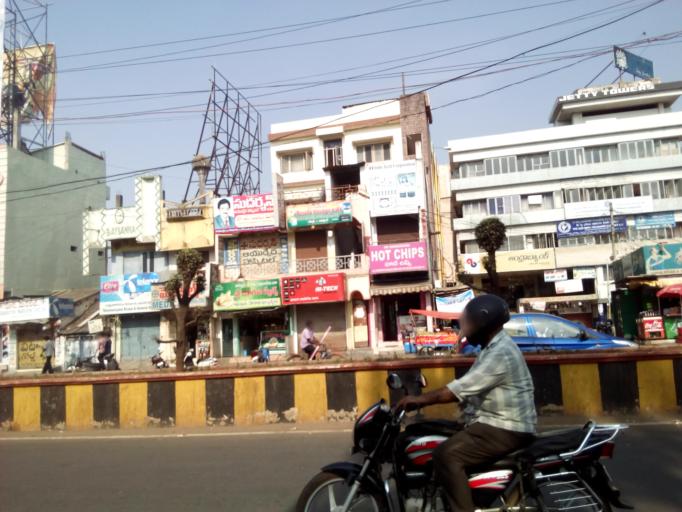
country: IN
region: Andhra Pradesh
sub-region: East Godavari
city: Rajahmundry
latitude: 16.9945
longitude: 81.7751
